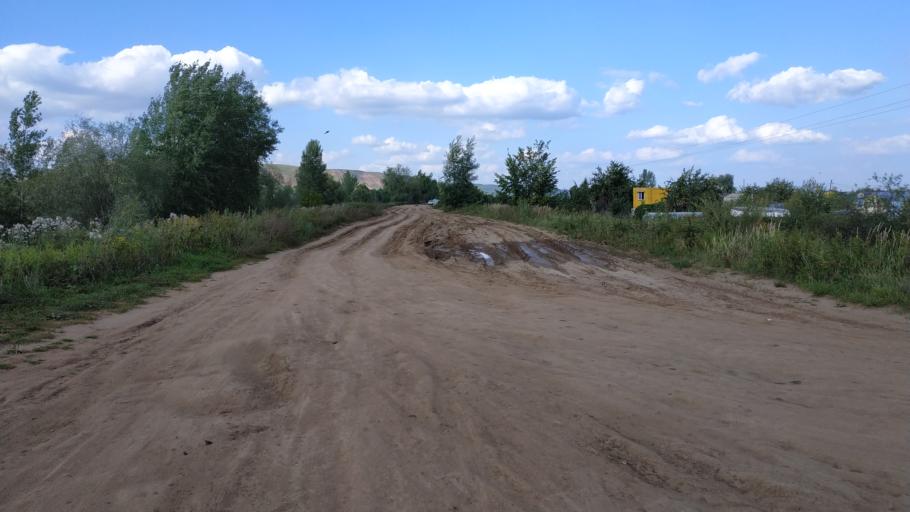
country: RU
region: Tatarstan
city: Nizhnekamsk
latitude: 55.6846
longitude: 51.7316
